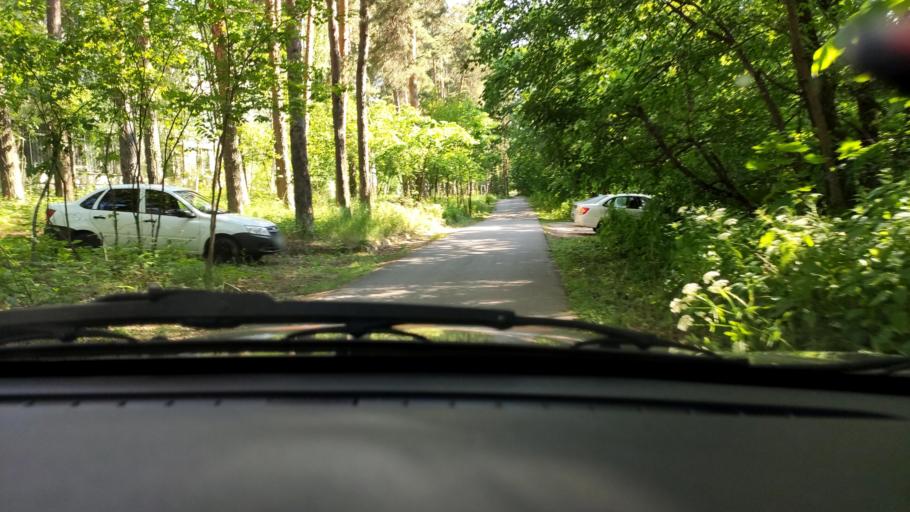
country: RU
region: Voronezj
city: Somovo
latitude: 51.8097
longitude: 39.3838
